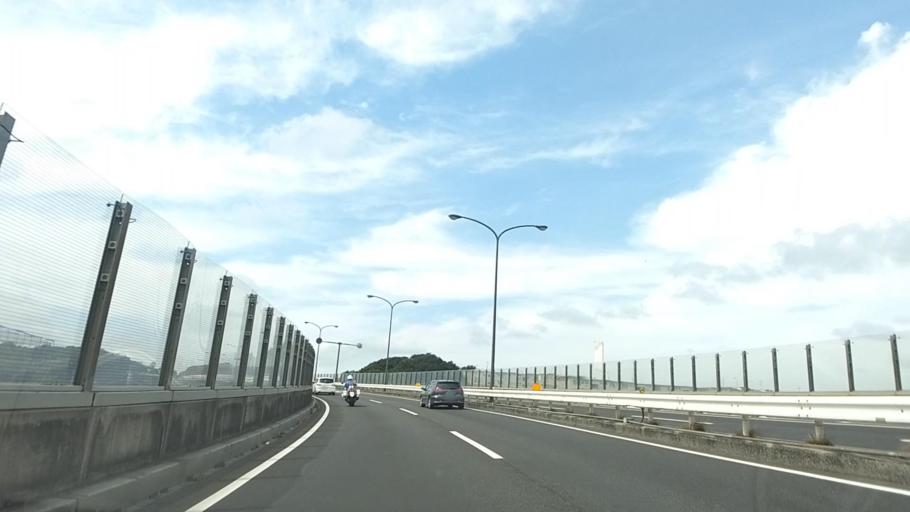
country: JP
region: Kanagawa
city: Yokohama
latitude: 35.4932
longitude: 139.5998
